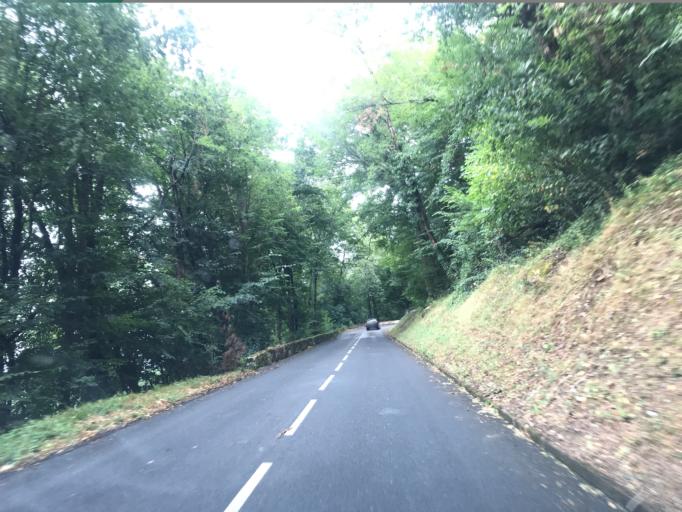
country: FR
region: Aquitaine
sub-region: Departement de la Dordogne
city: Domme
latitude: 44.8040
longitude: 1.2096
